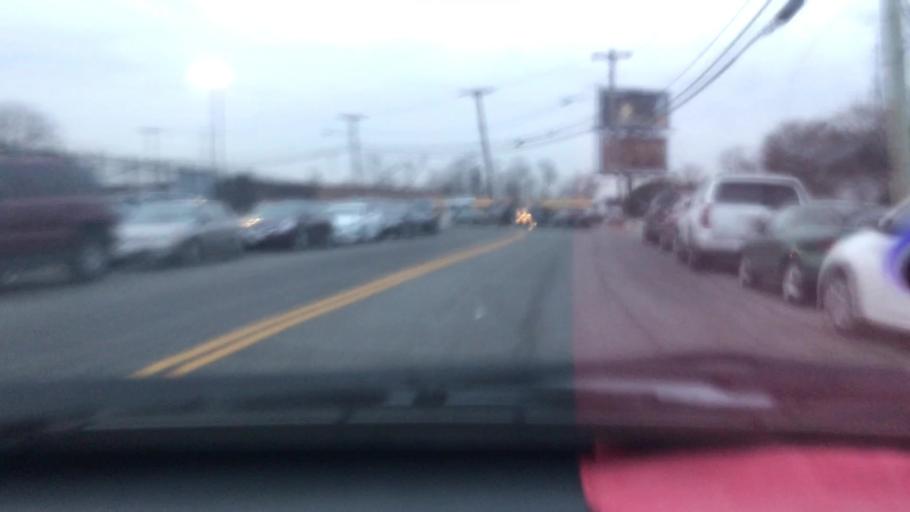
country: US
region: Maryland
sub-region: Prince George's County
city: Mount Rainier
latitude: 38.9196
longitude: -76.9699
